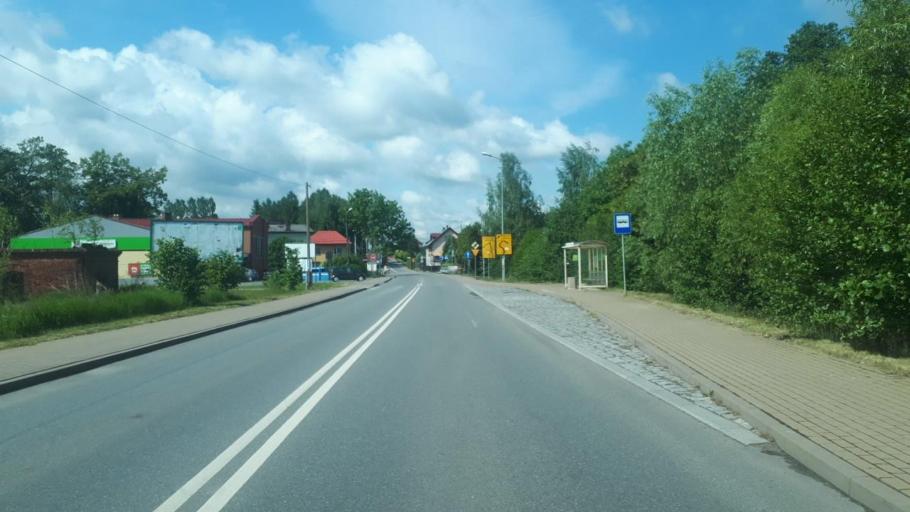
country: PL
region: Silesian Voivodeship
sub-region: Powiat bielski
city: Wilamowice
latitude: 49.9266
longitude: 19.1125
